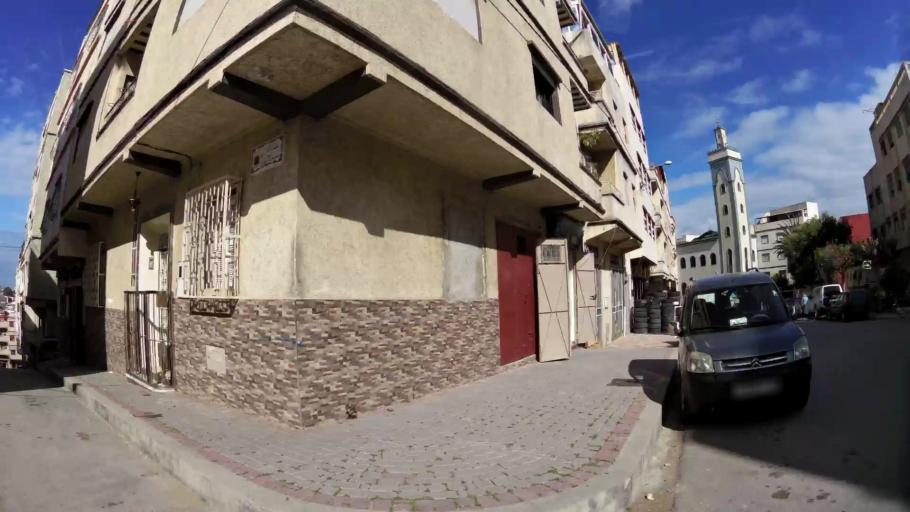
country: MA
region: Tanger-Tetouan
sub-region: Tanger-Assilah
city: Tangier
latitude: 35.7591
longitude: -5.8047
